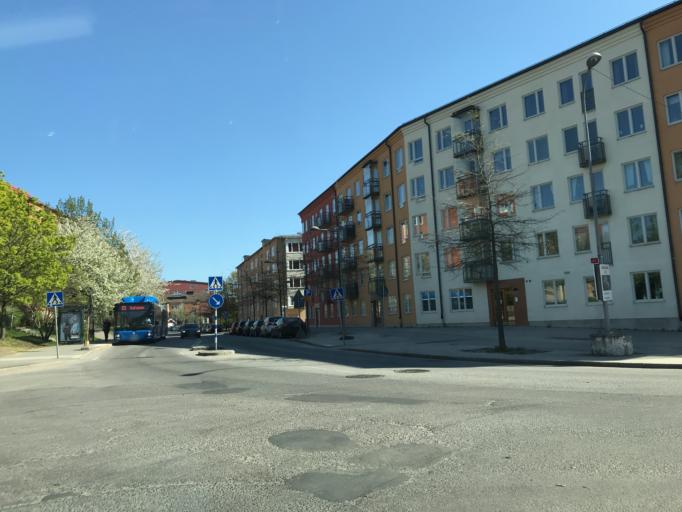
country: SE
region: Stockholm
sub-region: Huddinge Kommun
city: Huddinge
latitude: 59.2805
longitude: 18.0047
